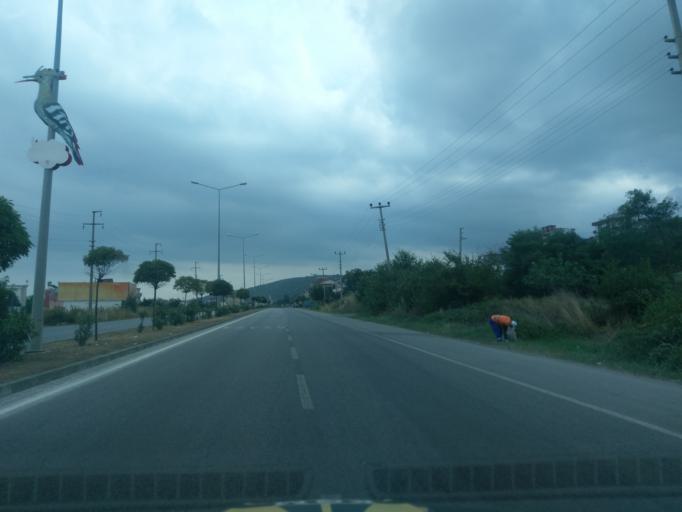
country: TR
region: Samsun
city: Taflan
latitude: 41.4121
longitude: 36.1754
